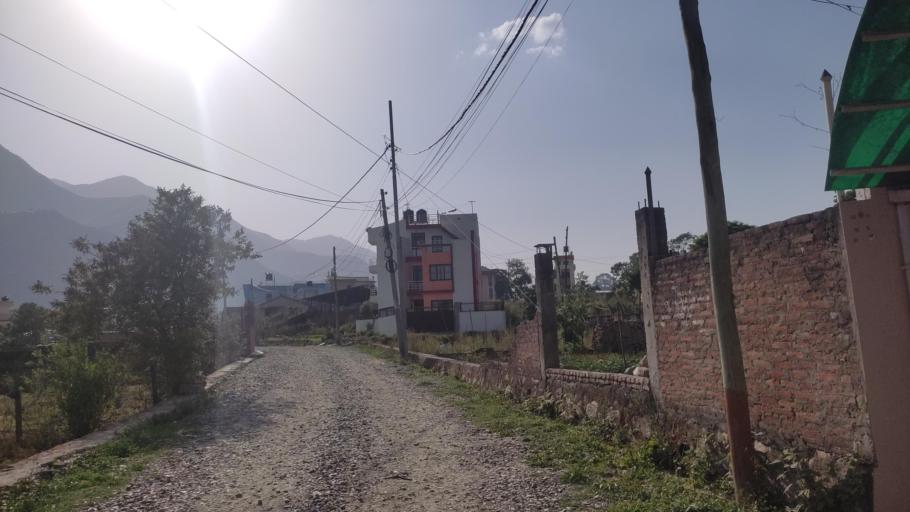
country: NP
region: Central Region
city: Kirtipur
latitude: 27.6563
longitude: 85.2860
